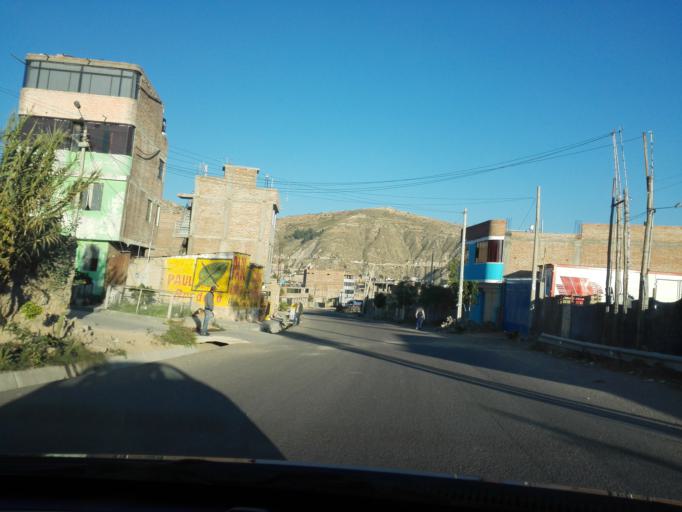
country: PE
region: Ayacucho
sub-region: Provincia de Huamanga
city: Ayacucho
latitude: -13.1363
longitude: -74.2239
